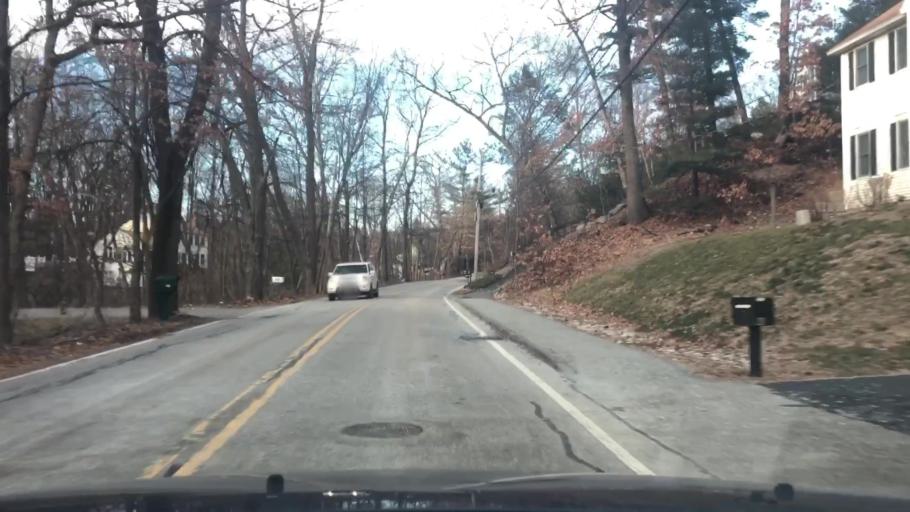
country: US
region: Massachusetts
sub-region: Essex County
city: Andover
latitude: 42.6682
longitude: -71.1101
